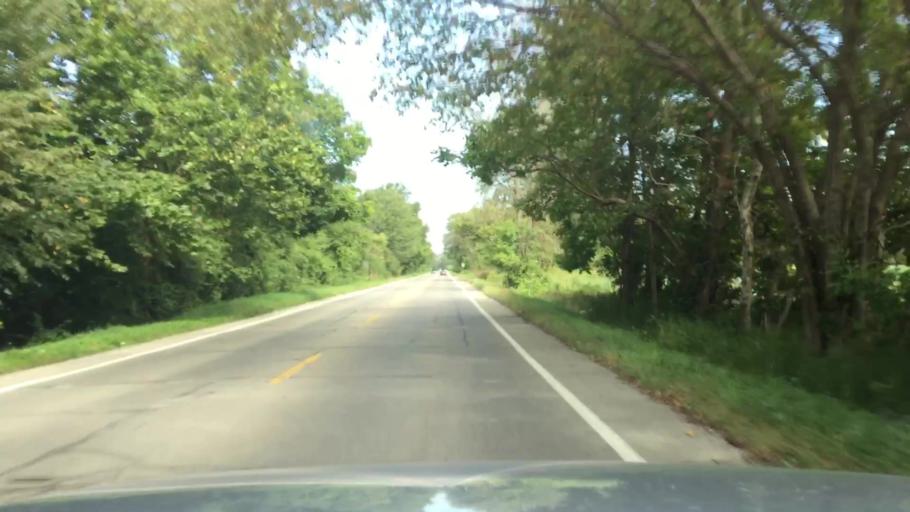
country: US
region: Michigan
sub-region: Wayne County
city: Belleville
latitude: 42.1832
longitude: -83.4832
